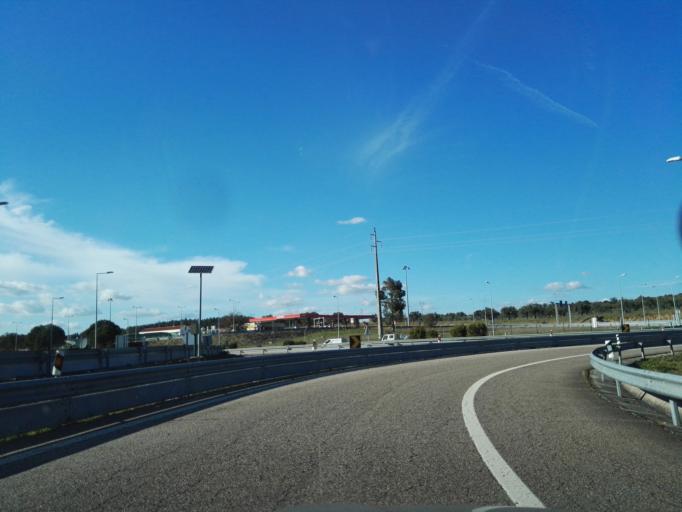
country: PT
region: Santarem
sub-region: Abrantes
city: Alferrarede
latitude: 39.4849
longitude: -8.1569
